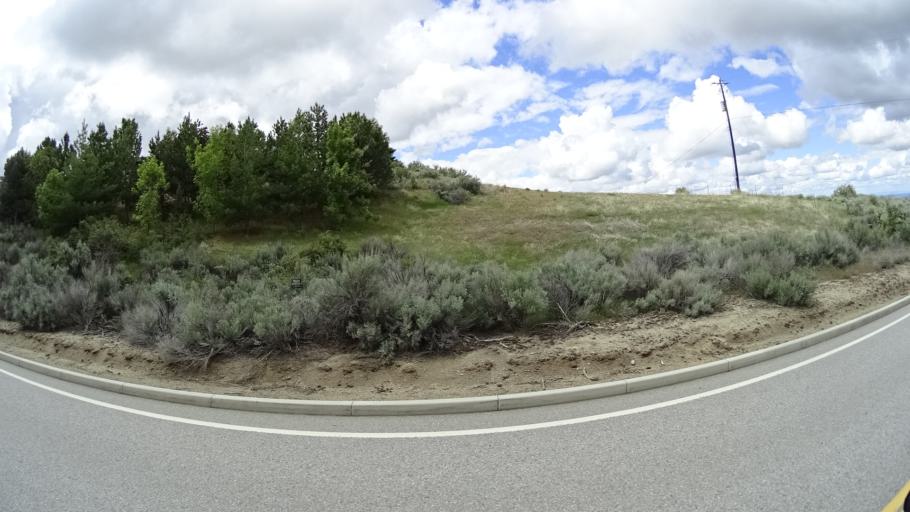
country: US
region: Idaho
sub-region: Ada County
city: Boise
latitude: 43.6942
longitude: -116.1765
